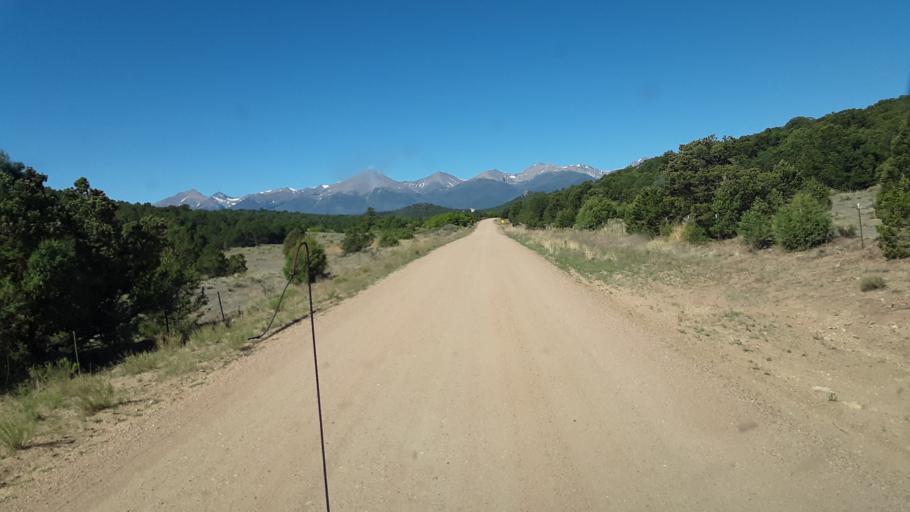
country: US
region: Colorado
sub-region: Custer County
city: Westcliffe
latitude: 38.2756
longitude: -105.5346
